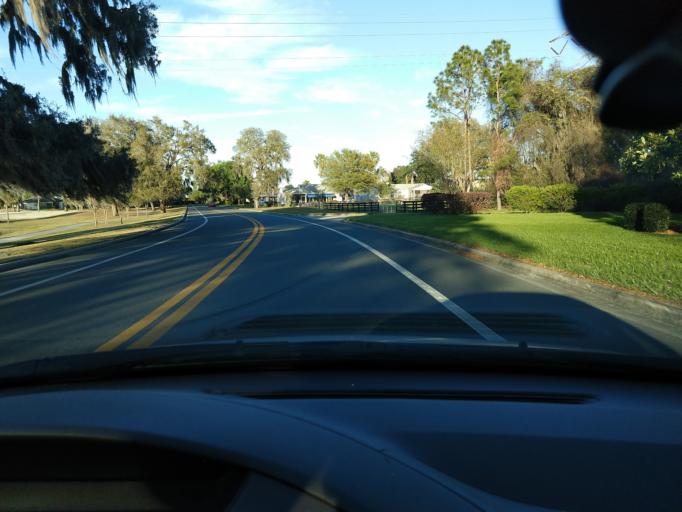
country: US
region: Florida
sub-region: Sumter County
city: The Villages
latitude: 28.9469
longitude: -81.9809
